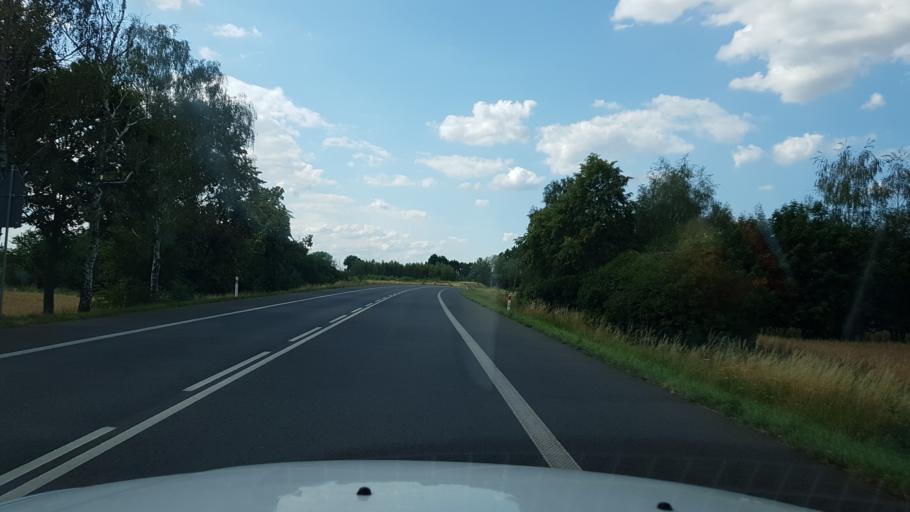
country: PL
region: West Pomeranian Voivodeship
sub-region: Powiat gryfinski
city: Stare Czarnowo
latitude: 53.2151
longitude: 14.8012
